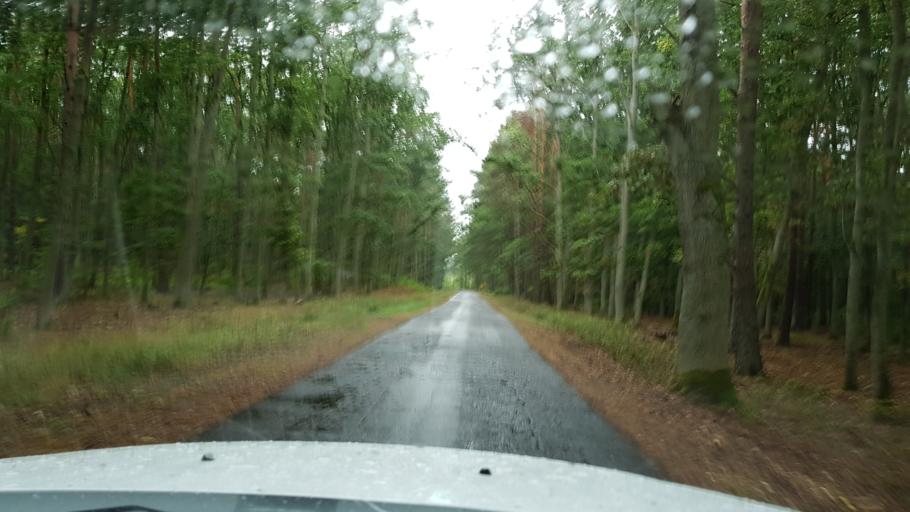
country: DE
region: Brandenburg
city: Schoneberg
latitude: 52.9603
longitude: 14.1970
